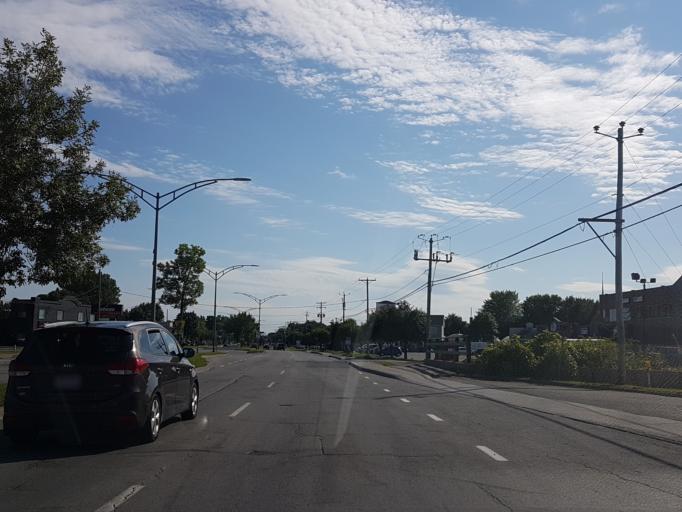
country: CA
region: Quebec
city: Sainte-Catherine
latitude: 46.3239
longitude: -72.5652
